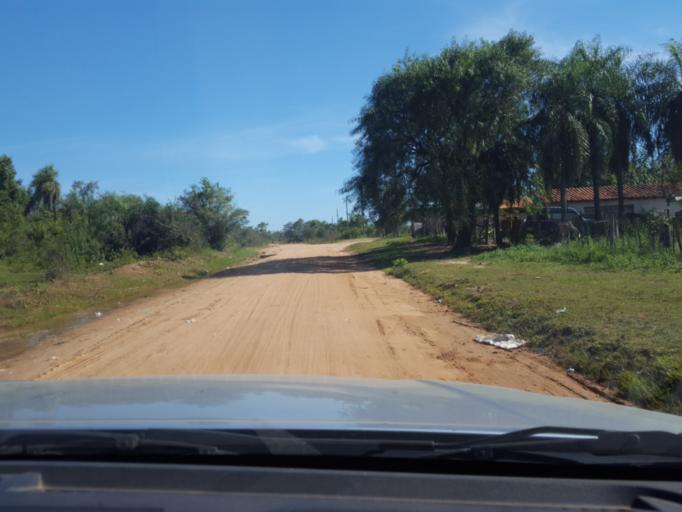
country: PY
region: Cordillera
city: Tobati
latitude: -25.2539
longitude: -57.1056
